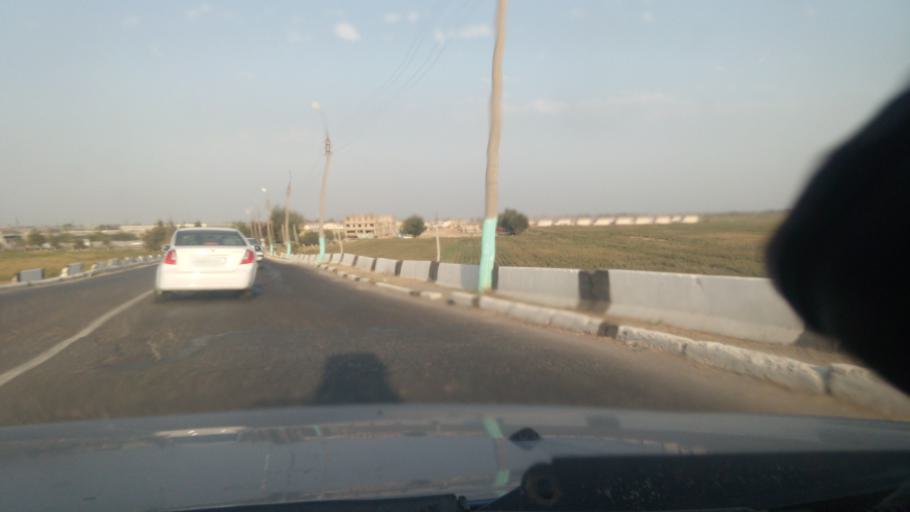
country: UZ
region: Sirdaryo
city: Guliston
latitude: 40.4746
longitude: 68.7728
